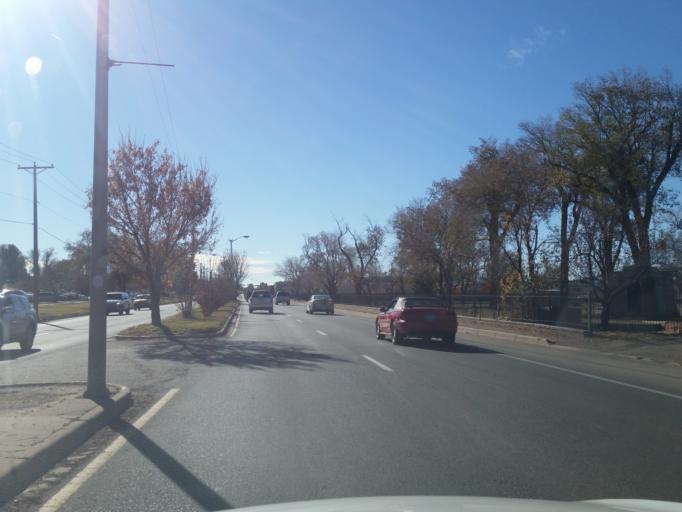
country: US
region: New Mexico
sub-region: Santa Fe County
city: Santa Fe
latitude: 35.6748
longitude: -105.9584
